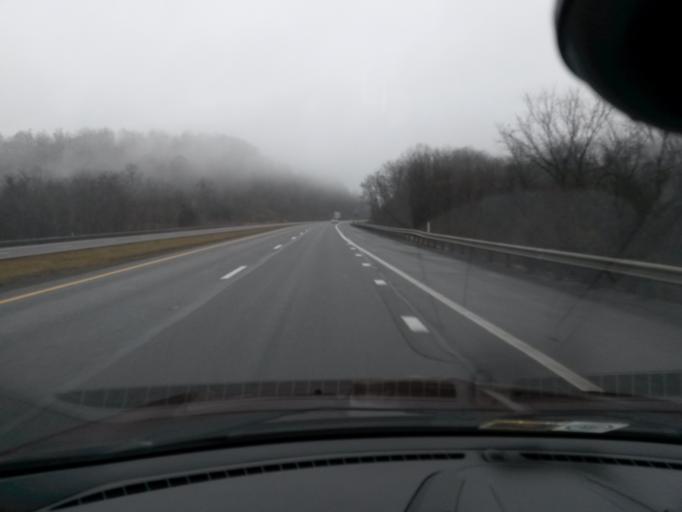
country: US
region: West Virginia
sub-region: Greenbrier County
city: Lewisburg
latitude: 37.8732
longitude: -80.5613
